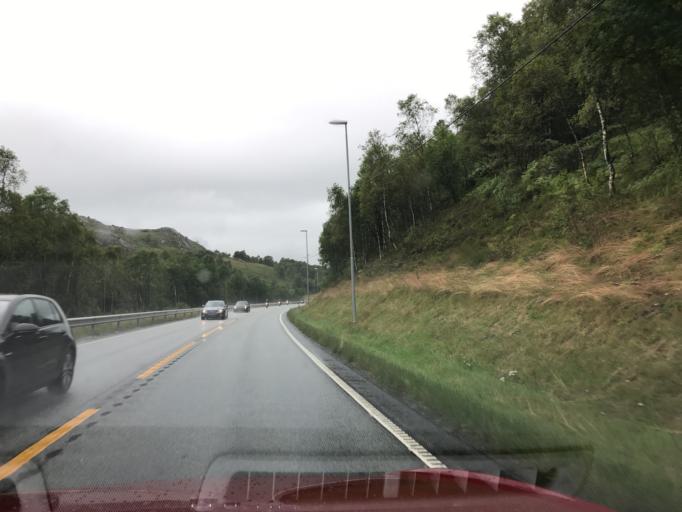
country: NO
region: Rogaland
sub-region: Bjerkreim
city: Vikesa
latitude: 58.5365
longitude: 6.0698
